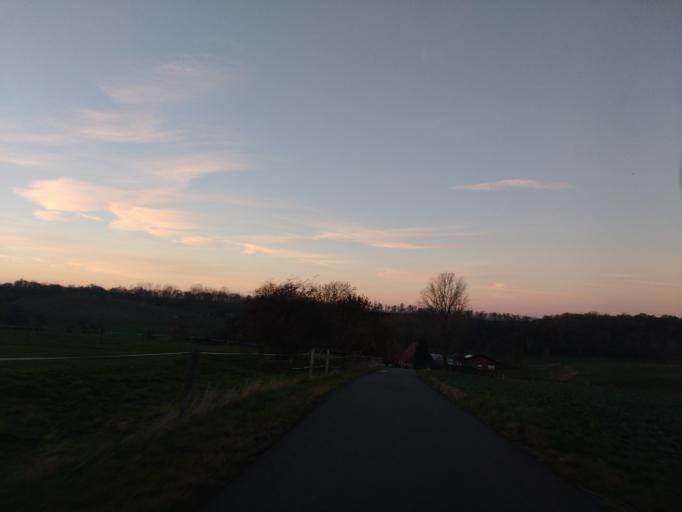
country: DE
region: North Rhine-Westphalia
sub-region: Regierungsbezirk Detmold
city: Paderborn
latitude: 51.6898
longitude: 8.7989
